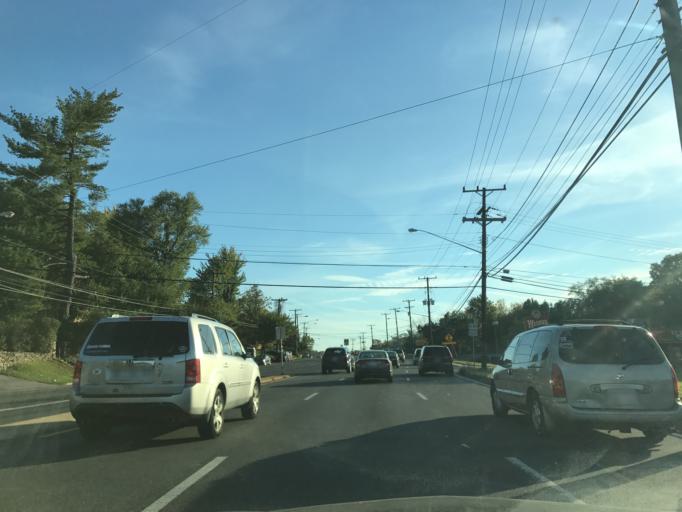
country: US
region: Maryland
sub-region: Prince George's County
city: East Riverdale
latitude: 38.9635
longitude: -76.9191
